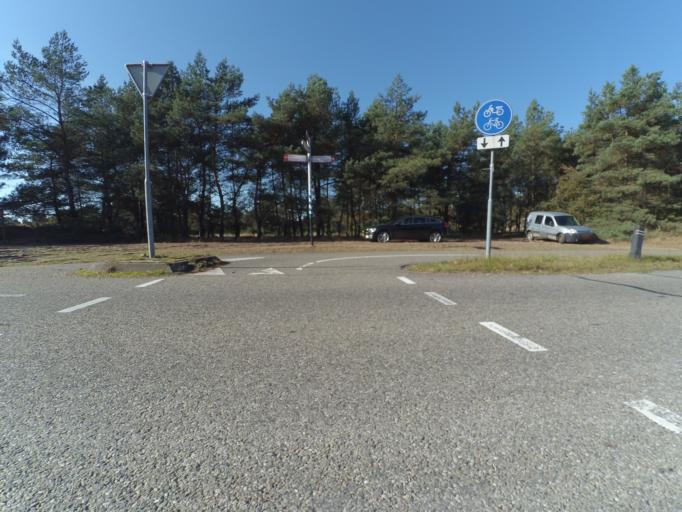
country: NL
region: Gelderland
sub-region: Gemeente Apeldoorn
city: Uddel
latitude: 52.1950
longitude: 5.7800
